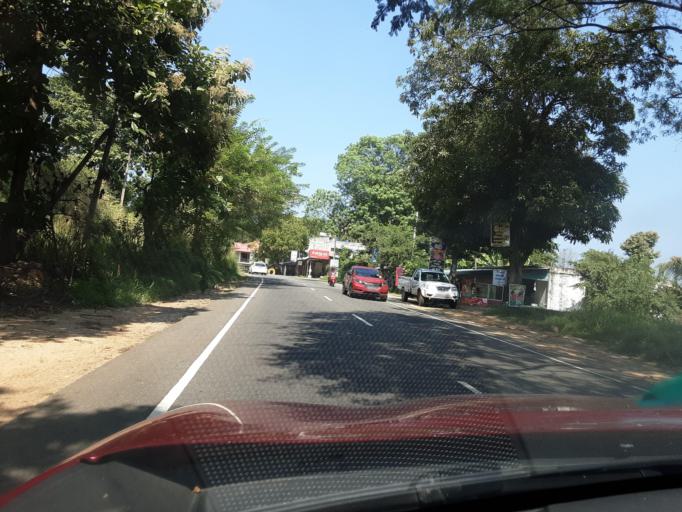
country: LK
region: Uva
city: Badulla
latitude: 7.2845
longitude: 81.0418
